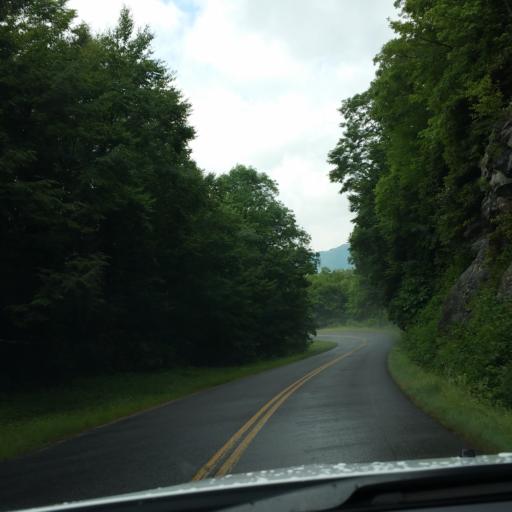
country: US
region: North Carolina
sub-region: Transylvania County
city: Brevard
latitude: 35.3469
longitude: -82.8056
